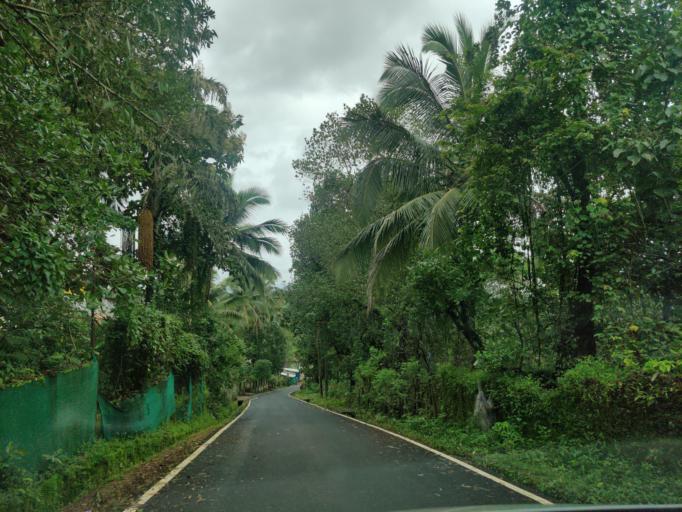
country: IN
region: Goa
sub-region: North Goa
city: Valpoy
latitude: 15.5276
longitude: 74.1406
